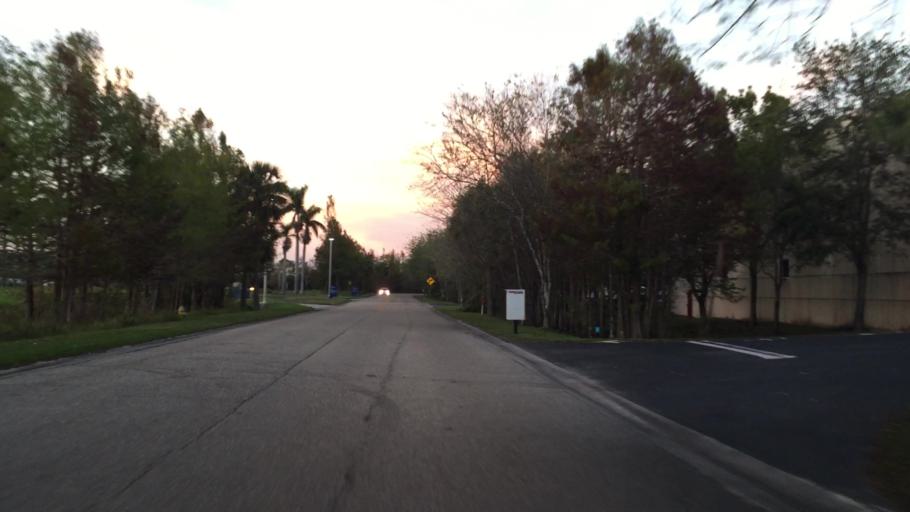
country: US
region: Florida
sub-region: Lee County
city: Gateway
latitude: 26.5367
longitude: -81.7915
